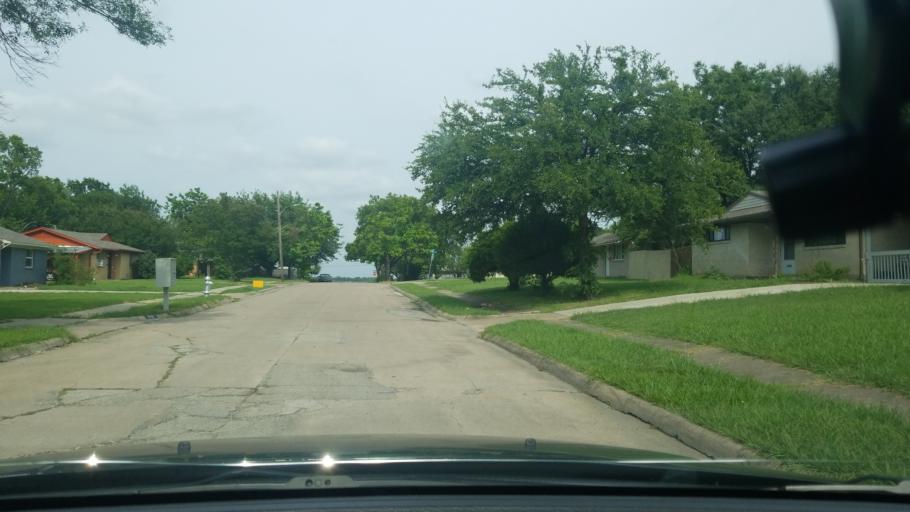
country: US
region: Texas
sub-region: Dallas County
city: Mesquite
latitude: 32.7600
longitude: -96.6243
